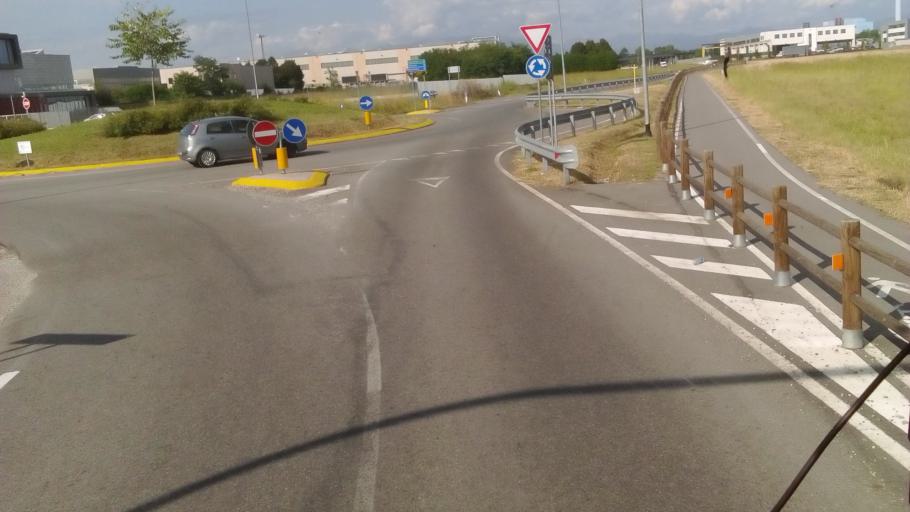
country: IT
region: Lombardy
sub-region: Citta metropolitana di Milano
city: Pozzo d'Adda
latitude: 45.5813
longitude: 9.5025
